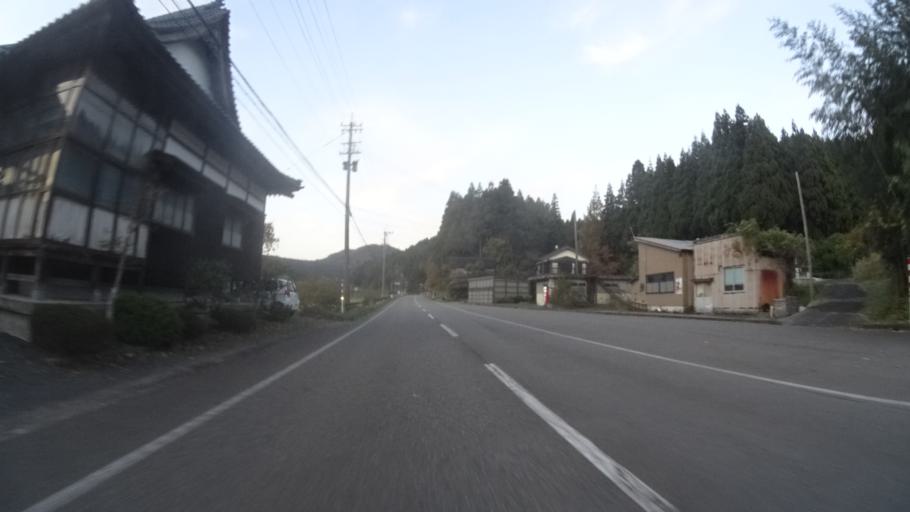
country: JP
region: Ishikawa
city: Nanao
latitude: 37.3025
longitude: 136.7986
